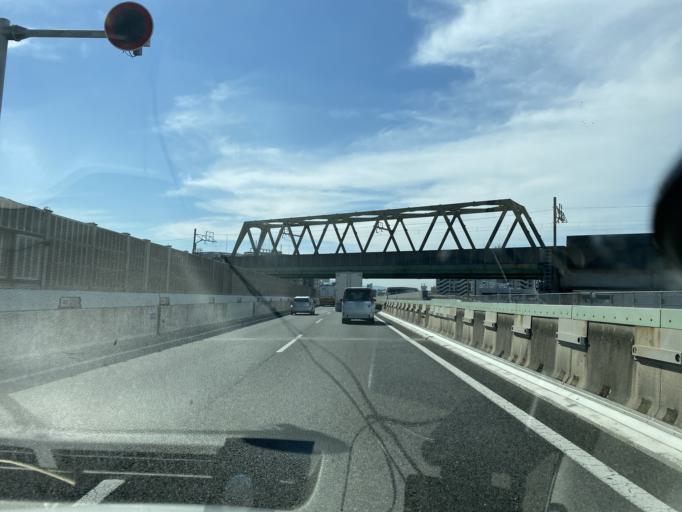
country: JP
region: Osaka
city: Ibaraki
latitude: 34.8060
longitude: 135.5626
